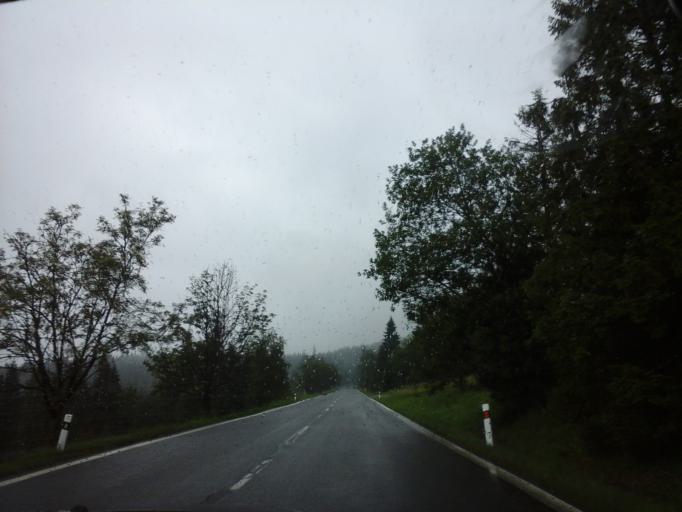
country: SK
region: Presovsky
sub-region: Okres Poprad
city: Zdiar
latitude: 49.2786
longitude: 20.2165
